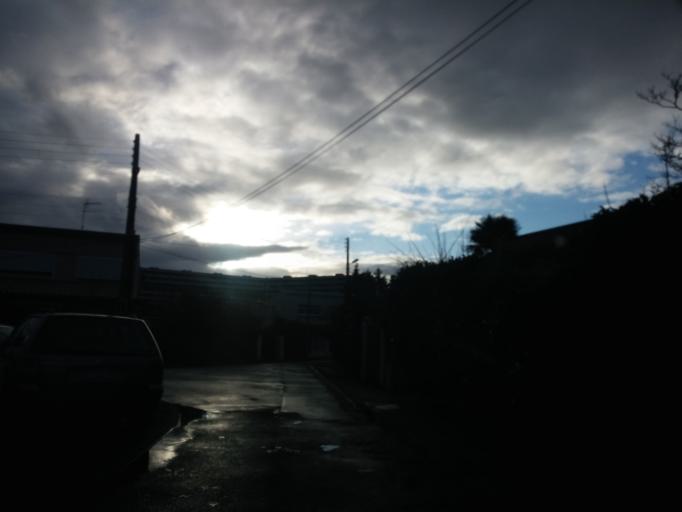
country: FR
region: Midi-Pyrenees
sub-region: Departement de la Haute-Garonne
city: Portet-sur-Garonne
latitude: 43.5705
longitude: 1.4102
